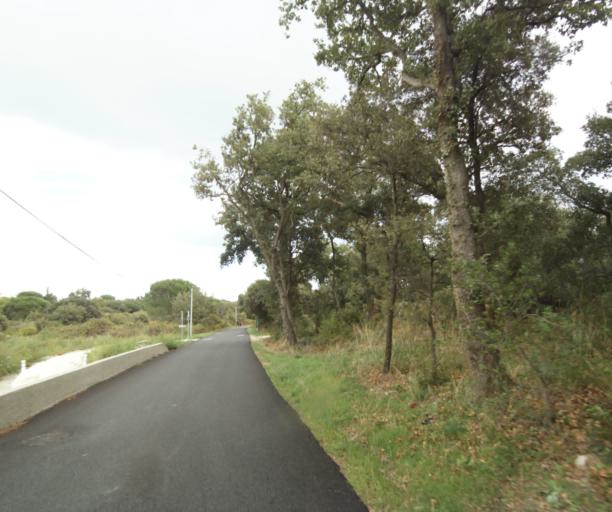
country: FR
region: Languedoc-Roussillon
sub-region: Departement des Pyrenees-Orientales
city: Argelers
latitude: 42.5413
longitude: 3.0070
